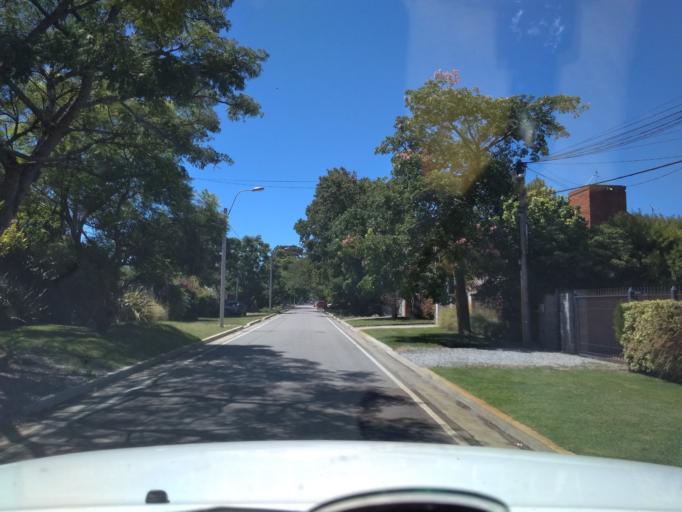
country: UY
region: Canelones
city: Barra de Carrasco
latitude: -34.8660
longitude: -56.0362
